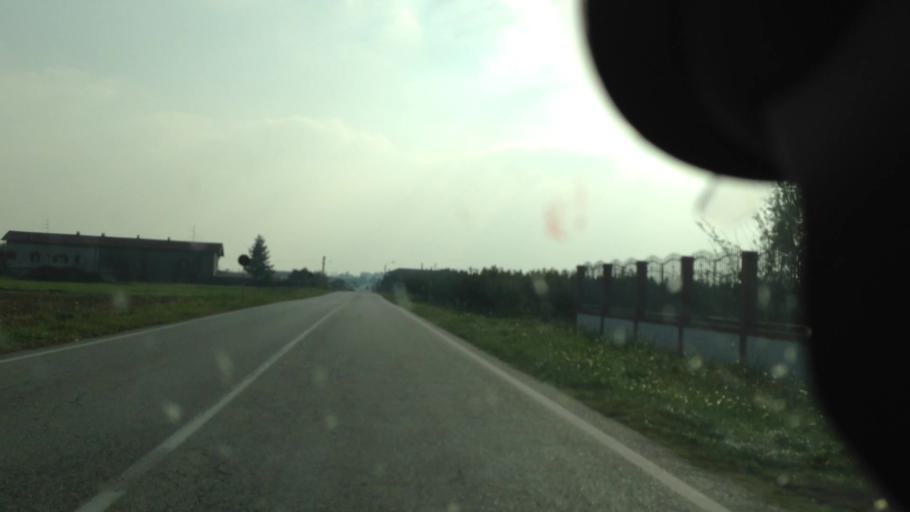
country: IT
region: Piedmont
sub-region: Provincia di Vercelli
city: Cigliano
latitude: 45.3266
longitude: 8.0362
